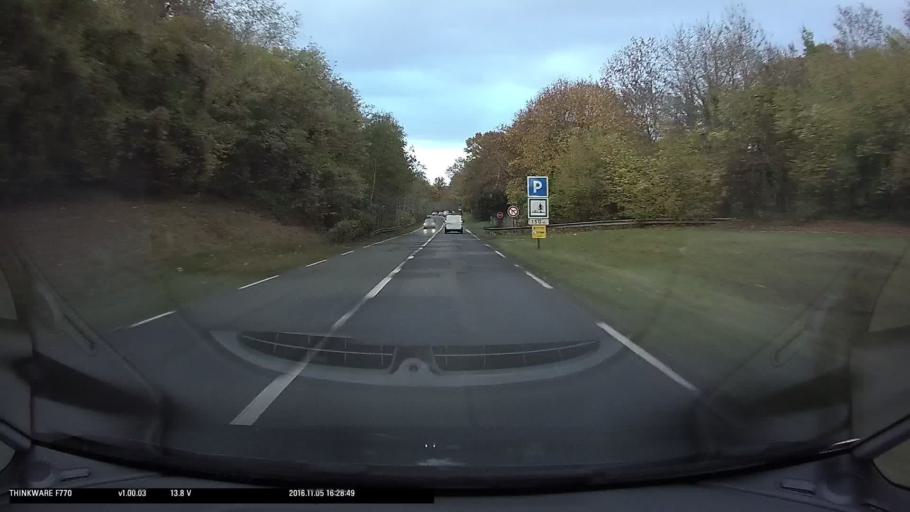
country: FR
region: Ile-de-France
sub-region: Departement du Val-d'Oise
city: Sagy
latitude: 49.0325
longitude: 1.9365
